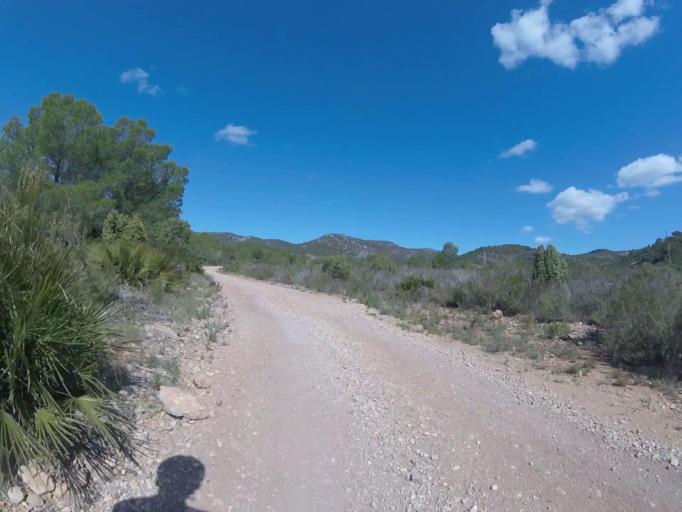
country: ES
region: Valencia
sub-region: Provincia de Castello
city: Alcoceber
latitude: 40.2864
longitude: 0.3207
